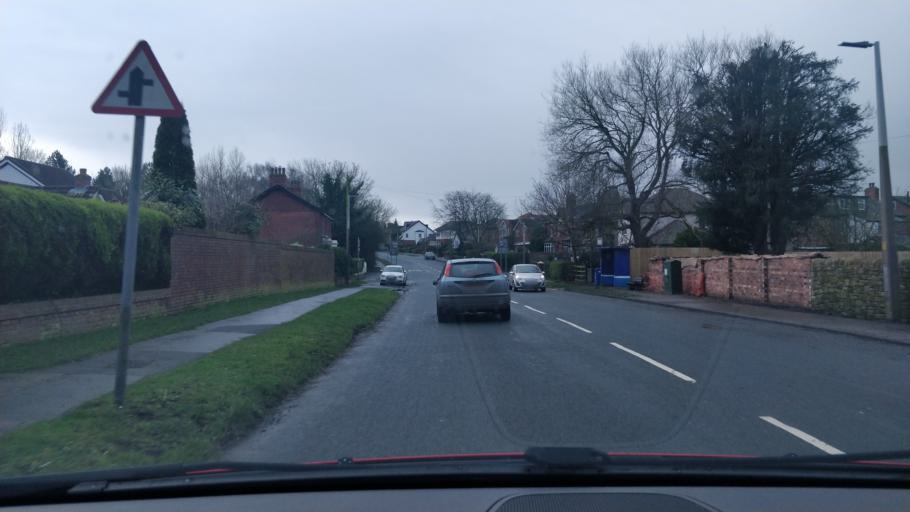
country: GB
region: England
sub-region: Lancashire
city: Tarleton
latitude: 53.7206
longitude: -2.7913
